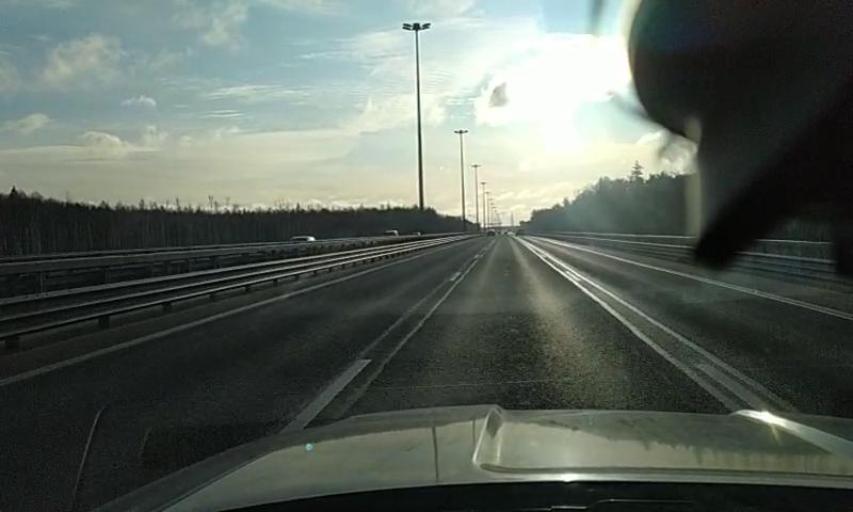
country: RU
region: St.-Petersburg
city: Pesochnyy
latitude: 60.1023
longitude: 30.0892
